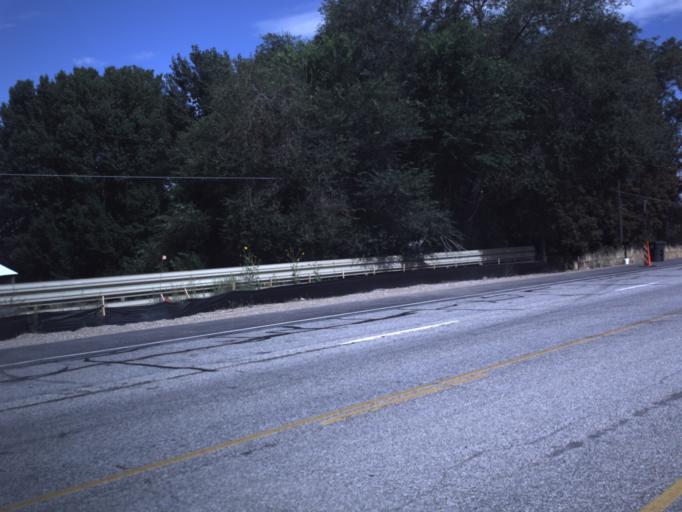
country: US
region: Utah
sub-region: Box Elder County
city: South Willard
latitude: 41.3789
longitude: -112.0326
